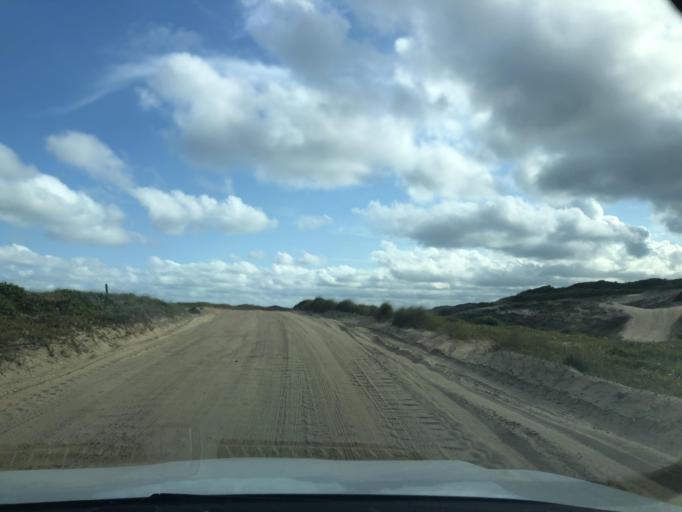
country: BR
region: Santa Catarina
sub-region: Sao Francisco Do Sul
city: Sao Francisco do Sul
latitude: -26.2590
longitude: -48.5183
